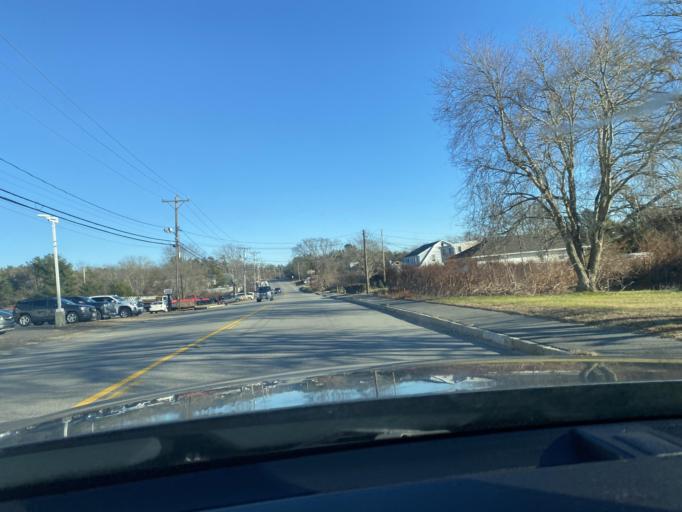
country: US
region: Massachusetts
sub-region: Plymouth County
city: Wareham Center
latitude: 41.7698
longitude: -70.7049
